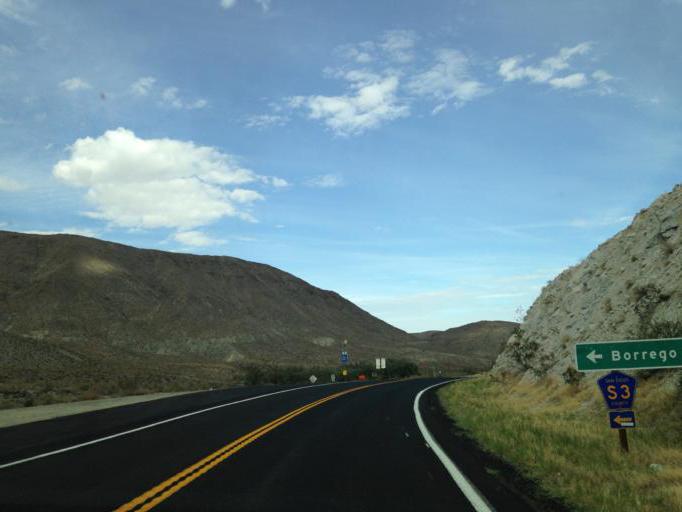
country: US
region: California
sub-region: San Diego County
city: Borrego Springs
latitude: 33.1353
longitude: -116.3812
